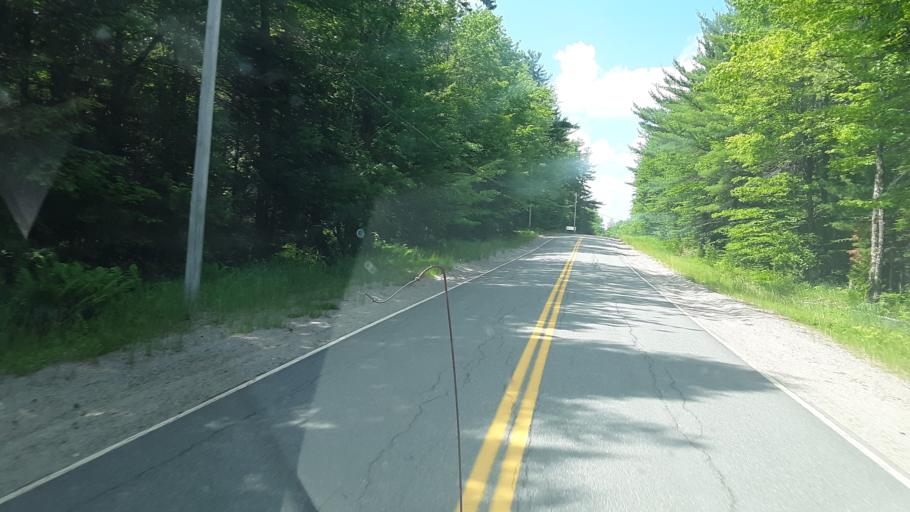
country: US
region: Maine
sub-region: Washington County
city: Machias
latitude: 44.9279
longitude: -67.6618
